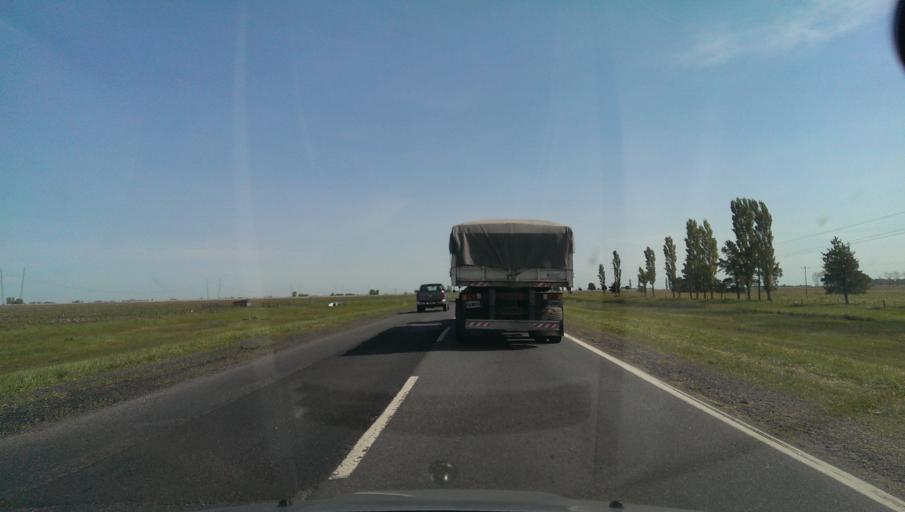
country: AR
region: Buenos Aires
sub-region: Partido de Azul
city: Azul
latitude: -36.6145
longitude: -59.6821
